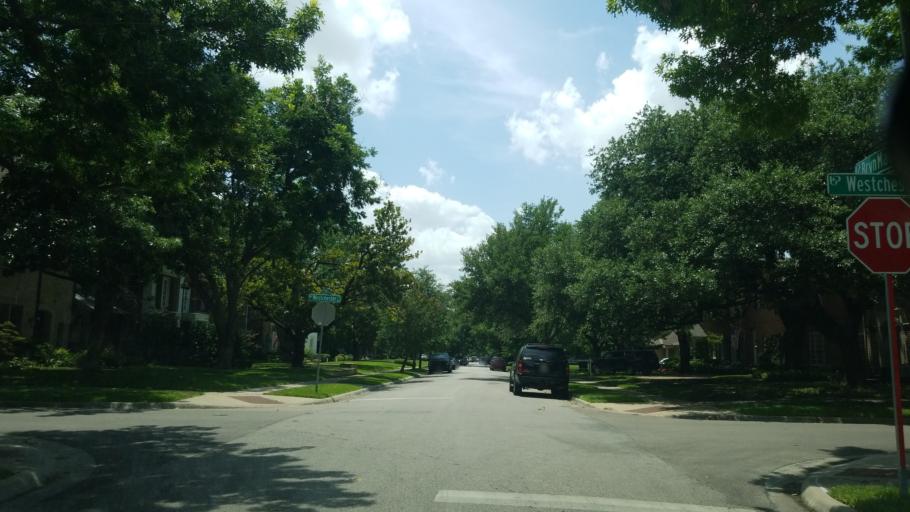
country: US
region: Texas
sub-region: Dallas County
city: University Park
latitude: 32.8559
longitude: -96.8063
